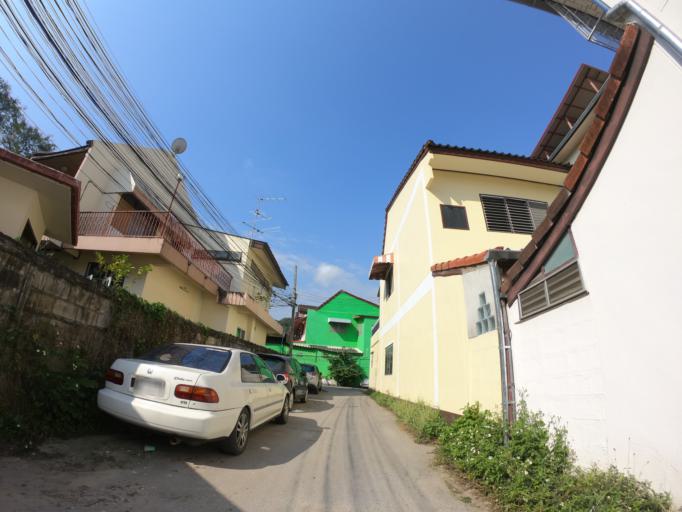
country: TH
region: Chiang Mai
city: Chiang Mai
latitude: 18.7886
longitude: 98.9575
